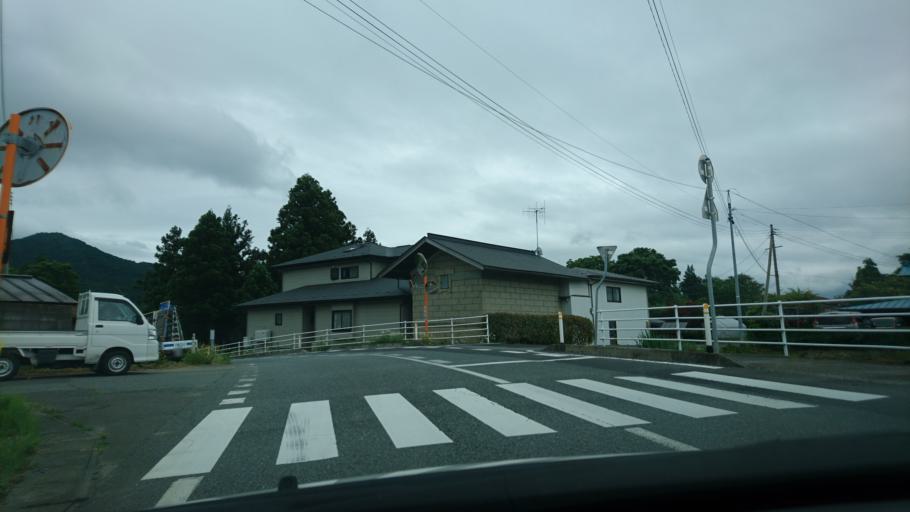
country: JP
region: Iwate
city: Ichinoseki
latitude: 38.9934
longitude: 141.1438
